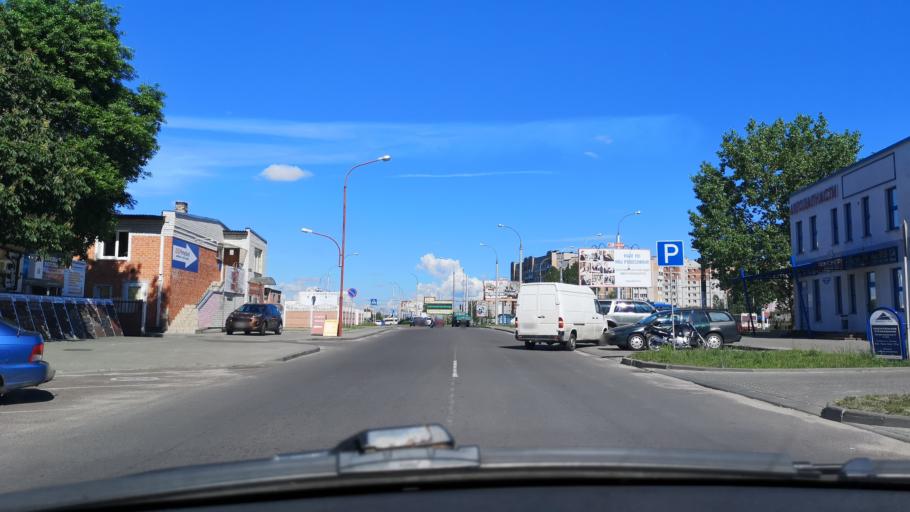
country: BY
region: Brest
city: Brest
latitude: 52.0688
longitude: 23.7527
